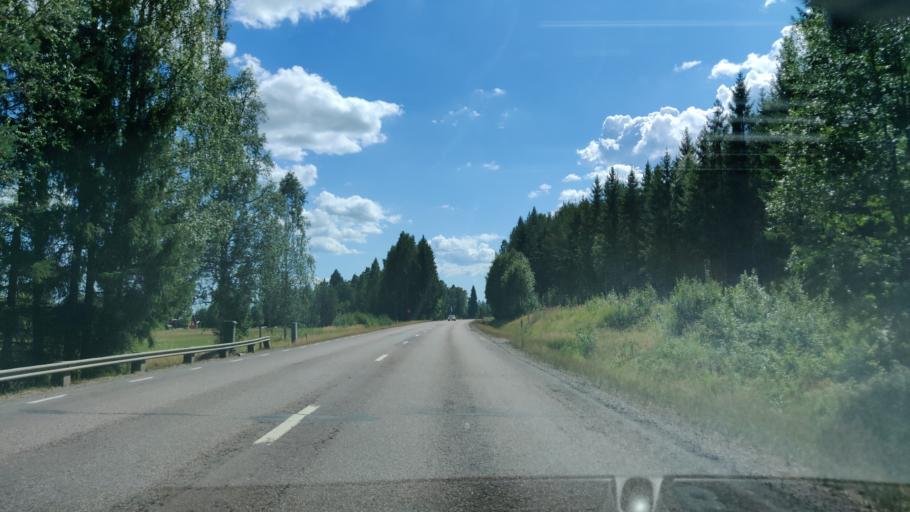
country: SE
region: Vaermland
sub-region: Hagfors Kommun
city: Ekshaerad
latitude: 60.1932
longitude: 13.4975
